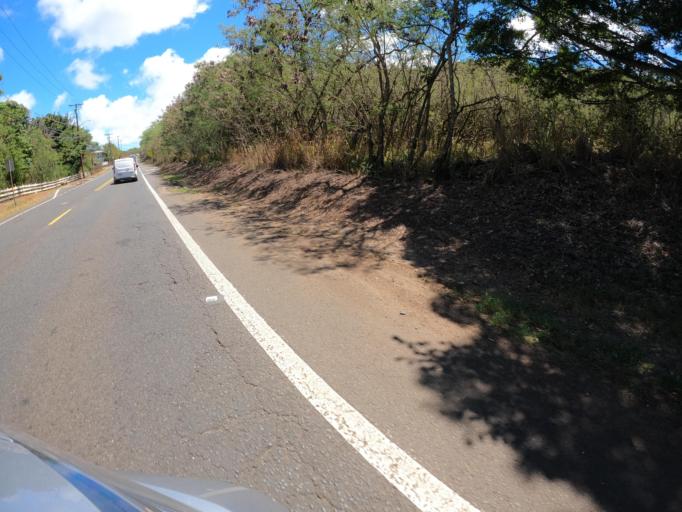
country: US
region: Hawaii
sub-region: Honolulu County
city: Pupukea
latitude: 21.6353
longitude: -158.0680
